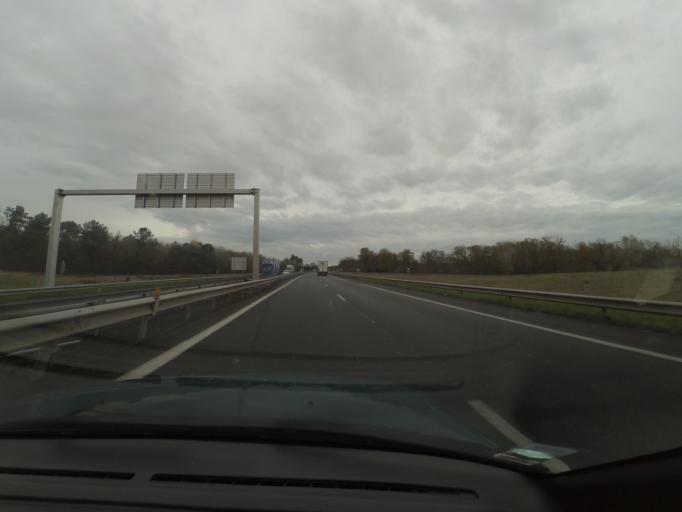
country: FR
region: Pays de la Loire
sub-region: Departement de Maine-et-Loire
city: Seiches-sur-le-Loir
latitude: 47.5440
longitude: -0.3401
